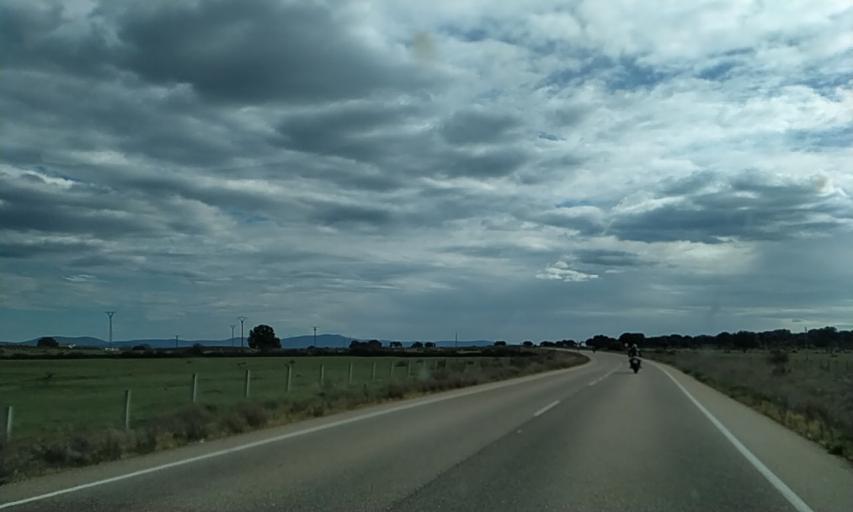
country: ES
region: Castille and Leon
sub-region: Provincia de Salamanca
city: Herguijuela de Ciudad Rodrigo
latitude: 40.4596
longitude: -6.5889
